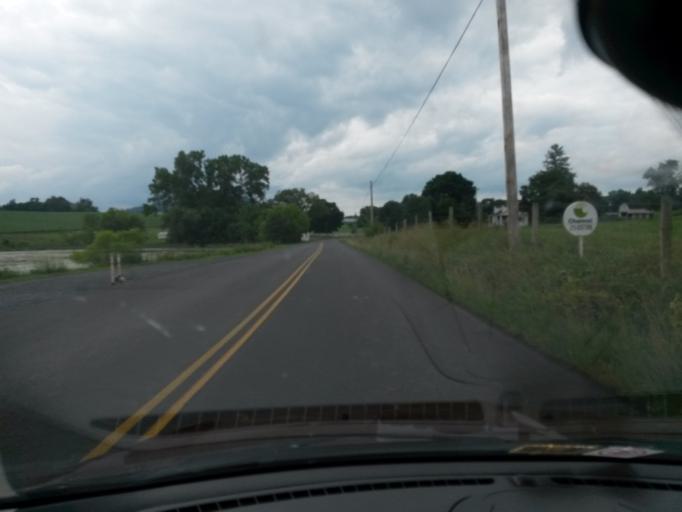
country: US
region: Virginia
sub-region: Rockingham County
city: Dayton
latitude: 38.4246
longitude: -78.9400
